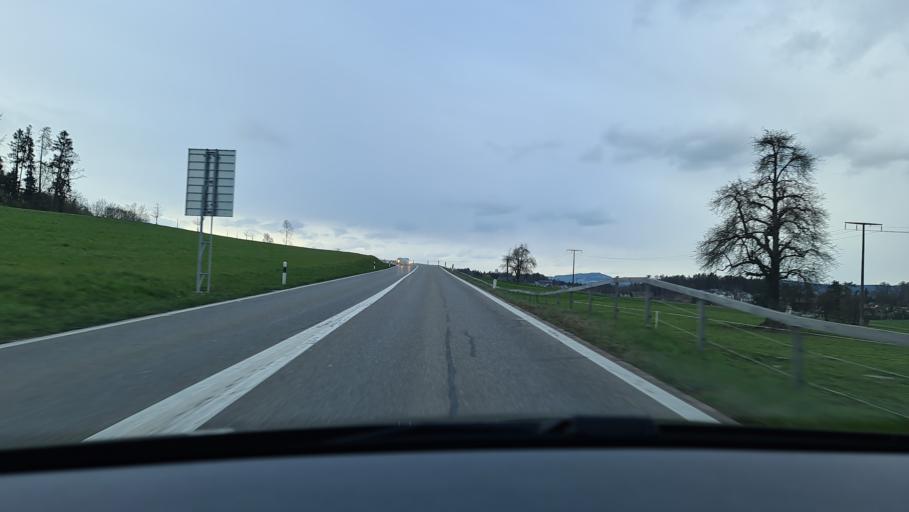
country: CH
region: Aargau
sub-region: Bezirk Muri
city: Merenschwand
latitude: 47.2393
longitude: 8.3638
